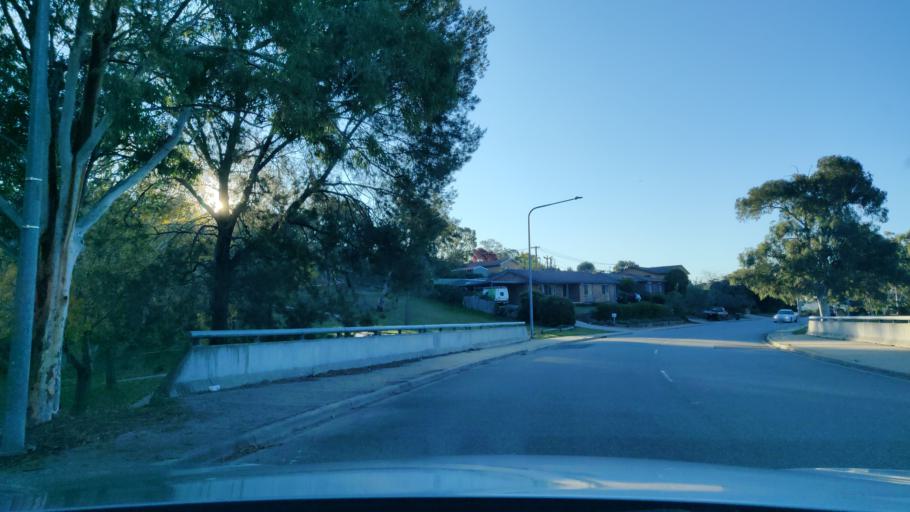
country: AU
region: Australian Capital Territory
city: Macarthur
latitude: -35.4493
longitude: 149.1212
